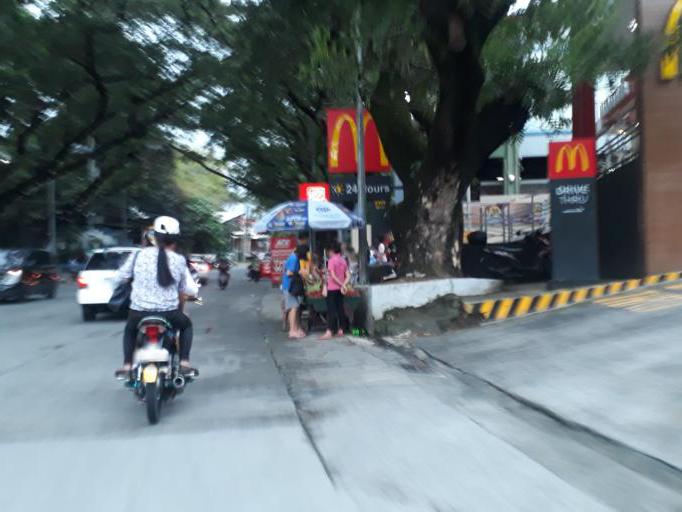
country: PH
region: Metro Manila
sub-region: Quezon City
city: Quezon City
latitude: 14.6843
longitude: 121.0779
